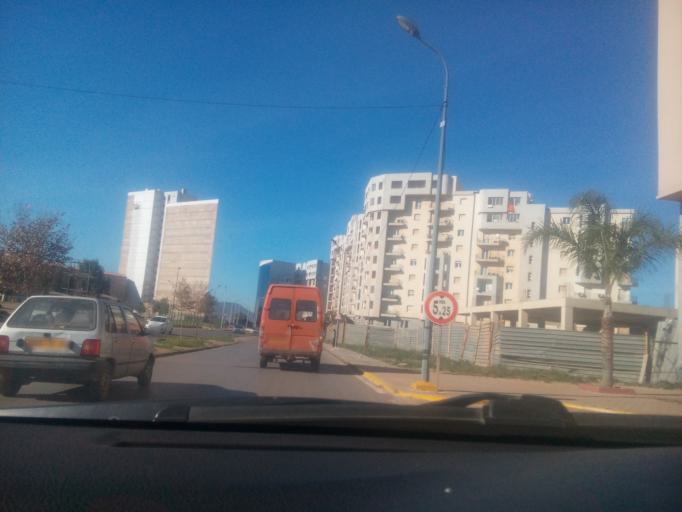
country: DZ
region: Oran
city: Oran
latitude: 35.7172
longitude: -0.5980
